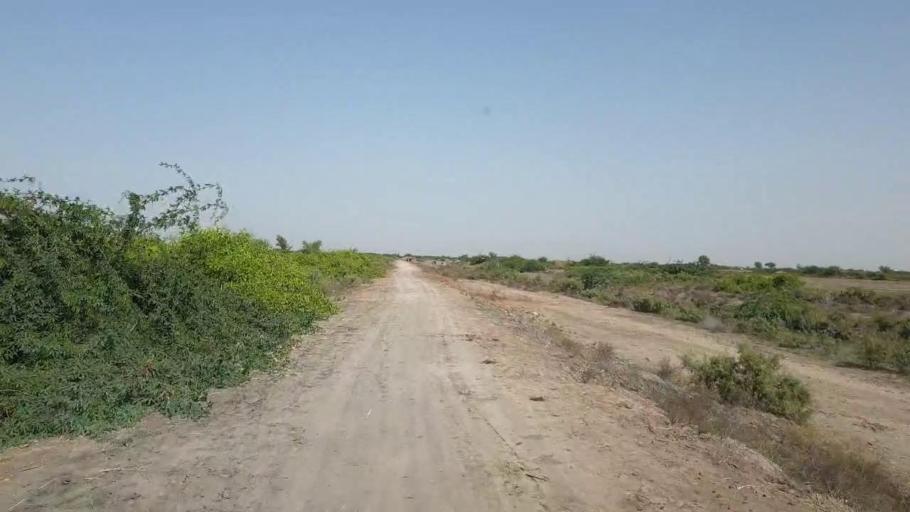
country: PK
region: Sindh
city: Tando Bago
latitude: 24.7053
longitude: 69.0711
